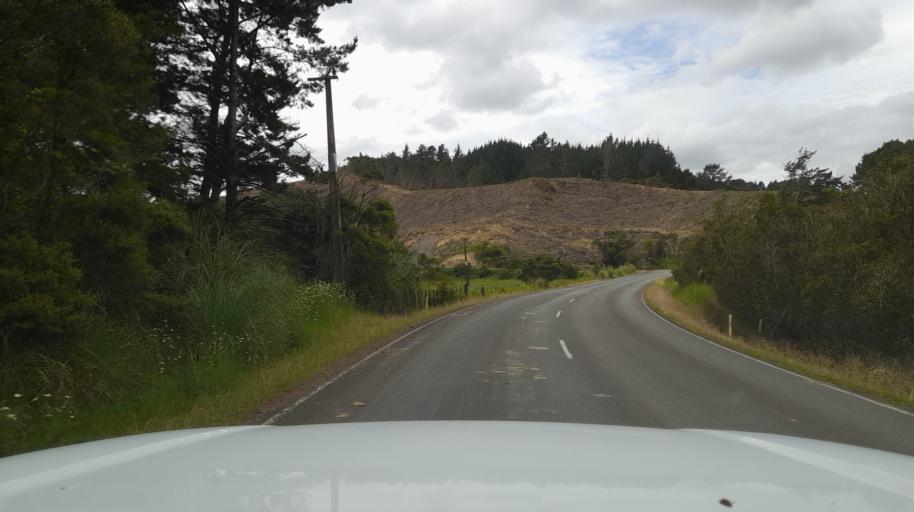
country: NZ
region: Northland
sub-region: Far North District
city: Kaitaia
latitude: -35.3617
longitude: 173.4448
